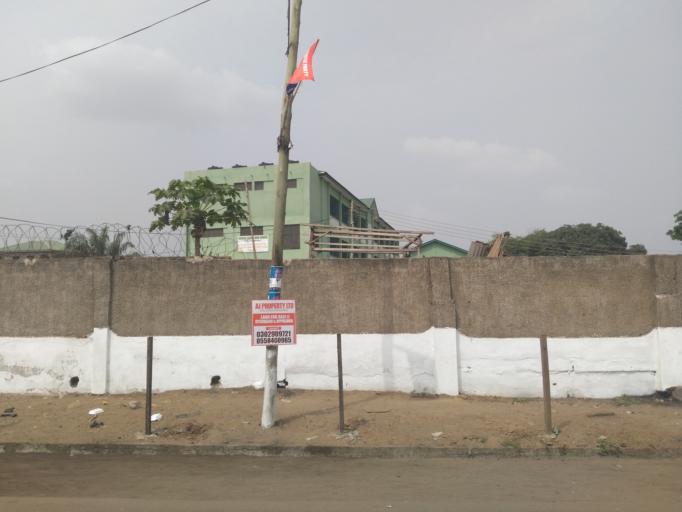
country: GH
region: Greater Accra
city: Nungua
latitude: 5.6024
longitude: -0.0791
